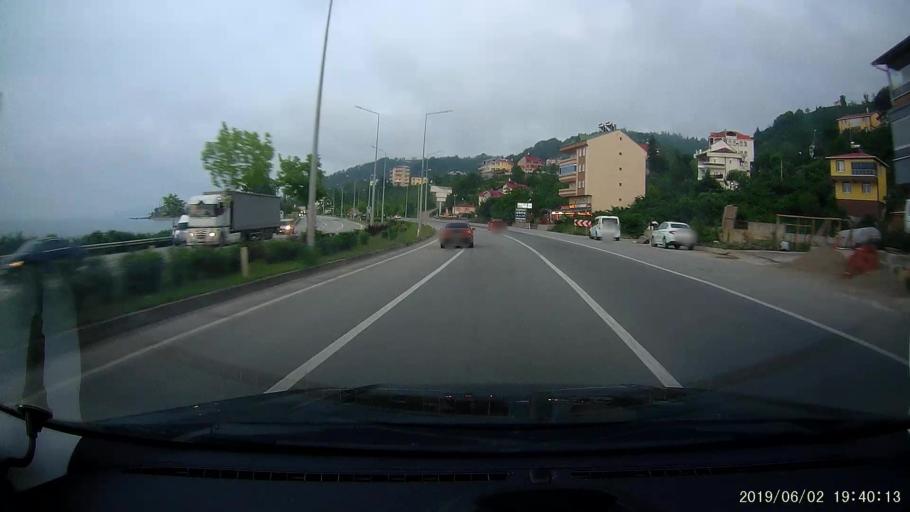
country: TR
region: Giresun
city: Kesap
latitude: 40.9149
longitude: 38.4552
